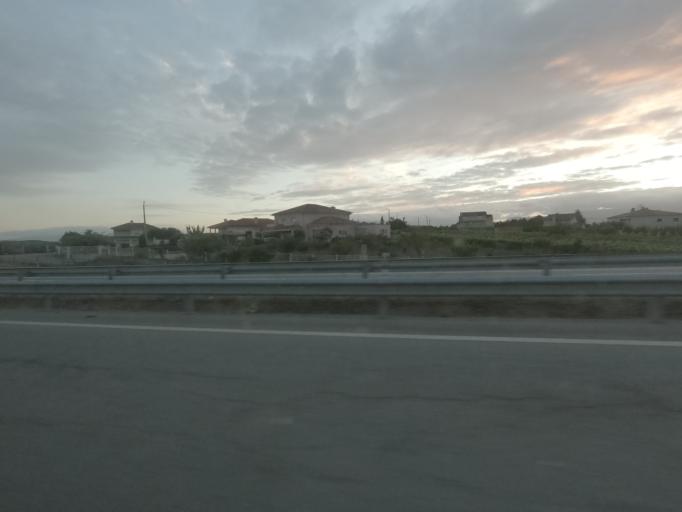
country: PT
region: Vila Real
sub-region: Vila Real
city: Vila Real
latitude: 41.2775
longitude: -7.6903
